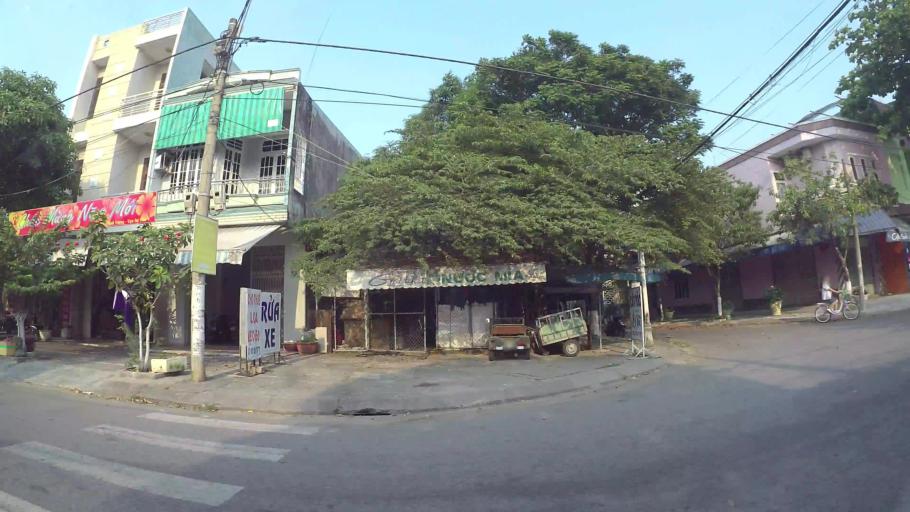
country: VN
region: Da Nang
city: Cam Le
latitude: 16.0190
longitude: 108.2072
